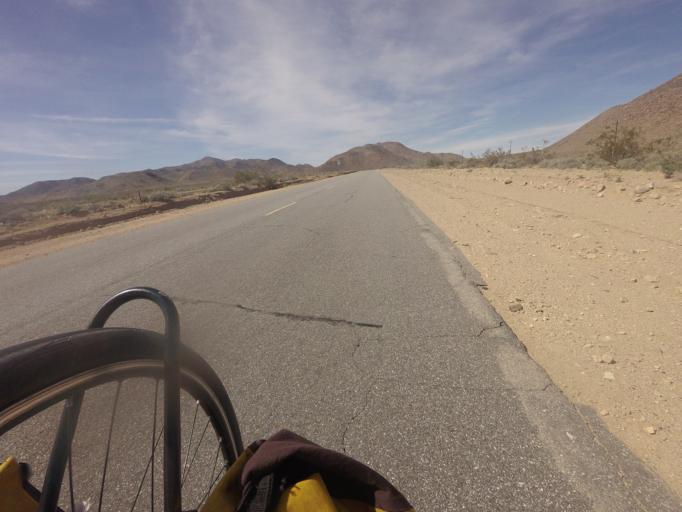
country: US
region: California
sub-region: San Bernardino County
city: Searles Valley
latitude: 35.5773
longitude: -117.4551
